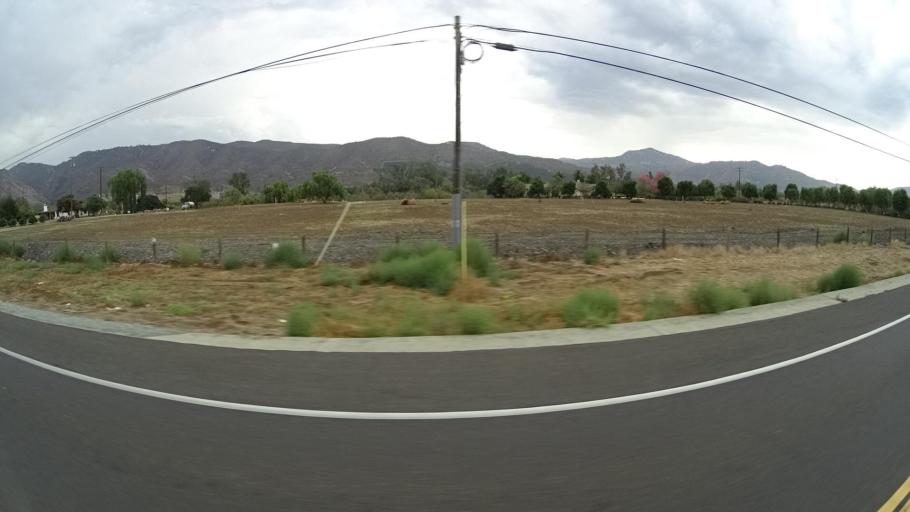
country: US
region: California
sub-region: San Diego County
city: San Pasqual
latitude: 33.0947
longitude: -116.9586
